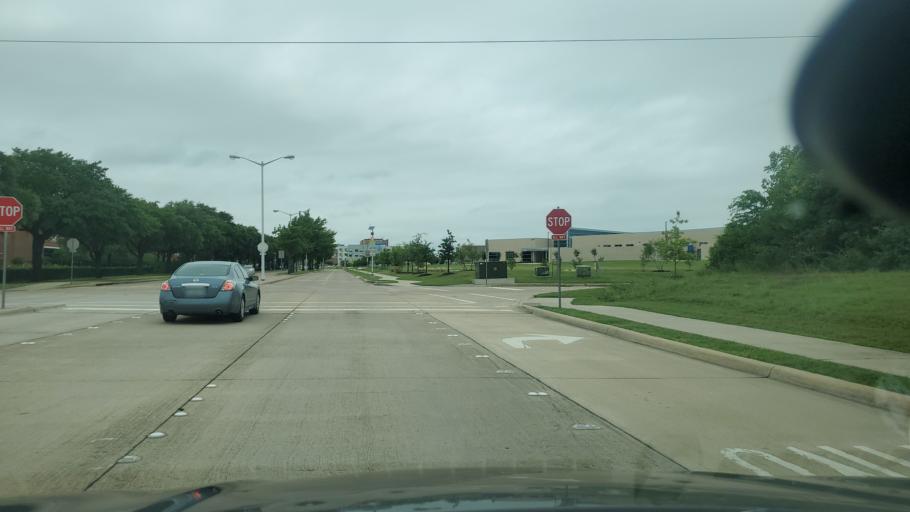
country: US
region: Texas
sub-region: Dallas County
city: Sachse
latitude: 32.9573
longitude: -96.6351
